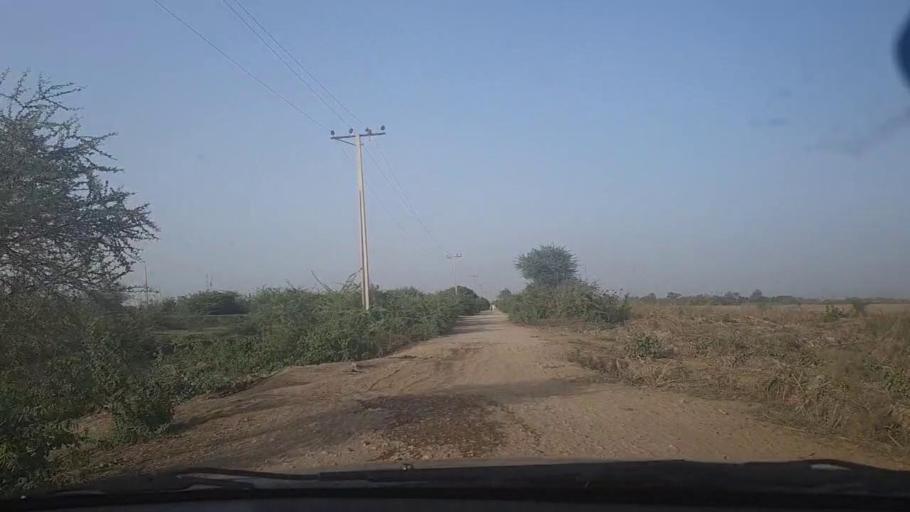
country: PK
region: Sindh
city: Keti Bandar
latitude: 24.2862
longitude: 67.6039
